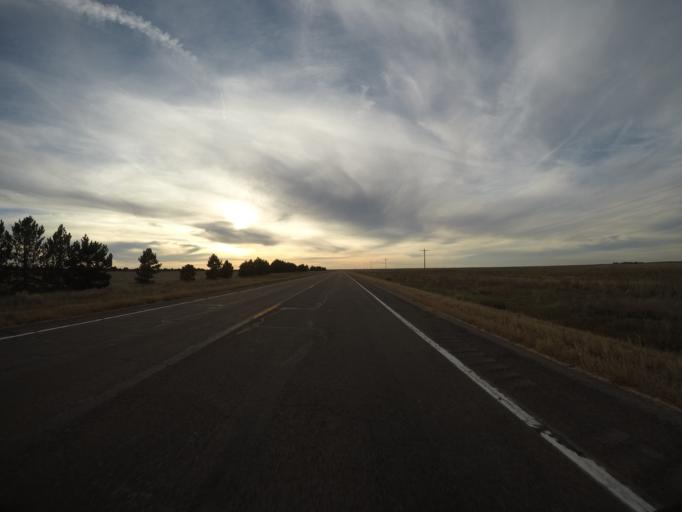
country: US
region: Colorado
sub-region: Yuma County
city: Yuma
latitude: 39.6700
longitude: -102.9096
